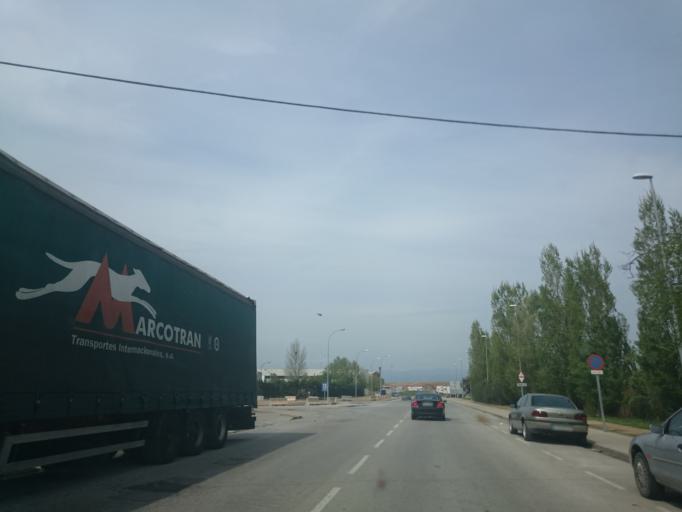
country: ES
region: Catalonia
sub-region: Provincia de Girona
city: Vilabertran
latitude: 42.2679
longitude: 2.9772
